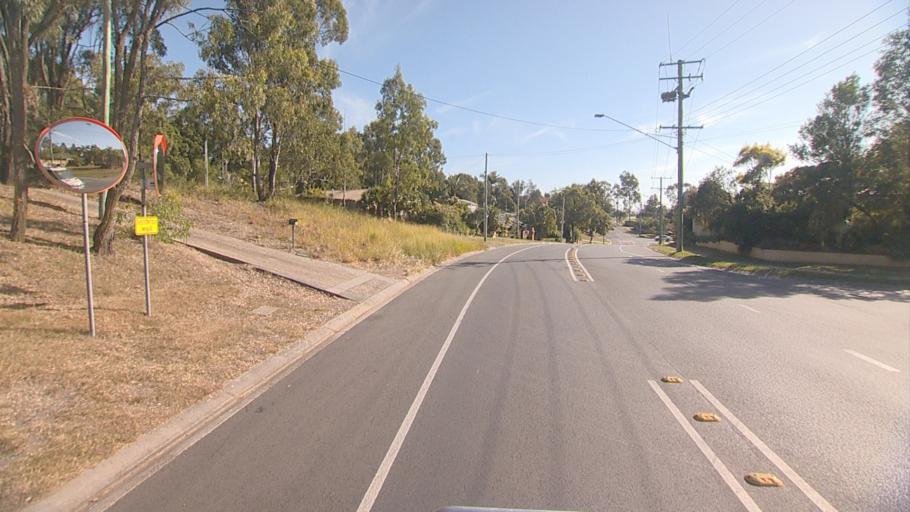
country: AU
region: Queensland
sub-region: Logan
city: Beenleigh
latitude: -27.7088
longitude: 153.1702
